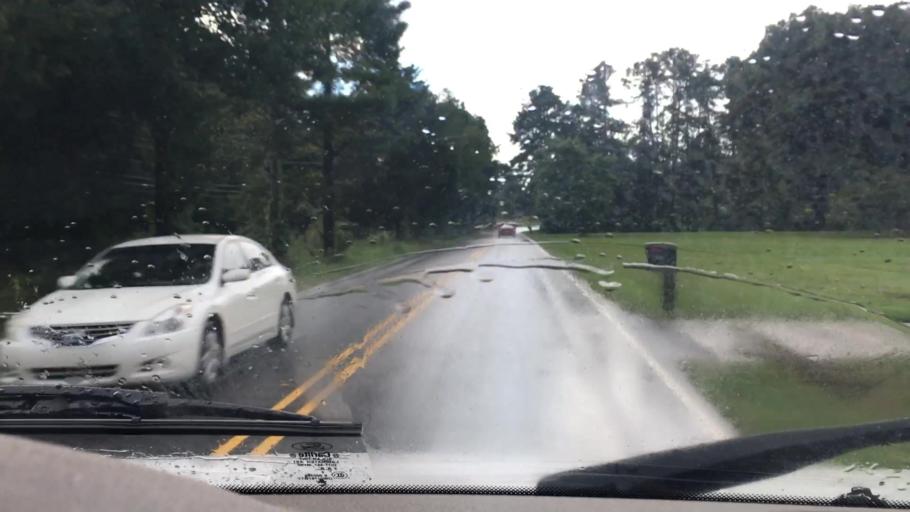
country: US
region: North Carolina
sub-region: Mecklenburg County
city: Huntersville
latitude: 35.4186
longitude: -80.9111
